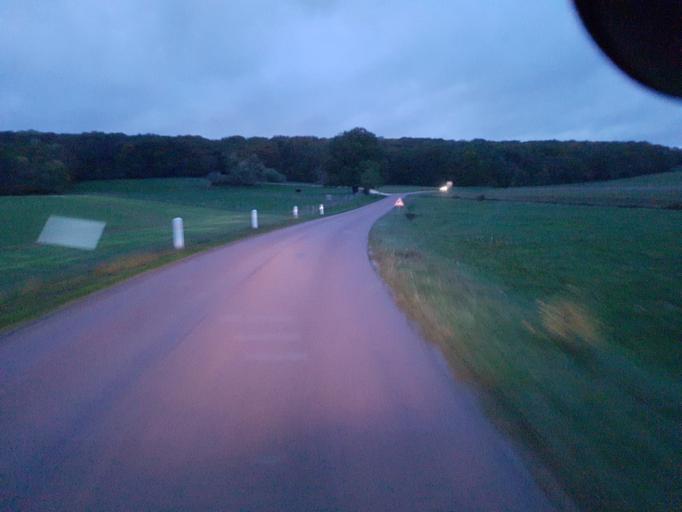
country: FR
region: Champagne-Ardenne
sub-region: Departement de l'Aube
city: Bar-sur-Seine
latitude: 48.1832
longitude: 4.3378
